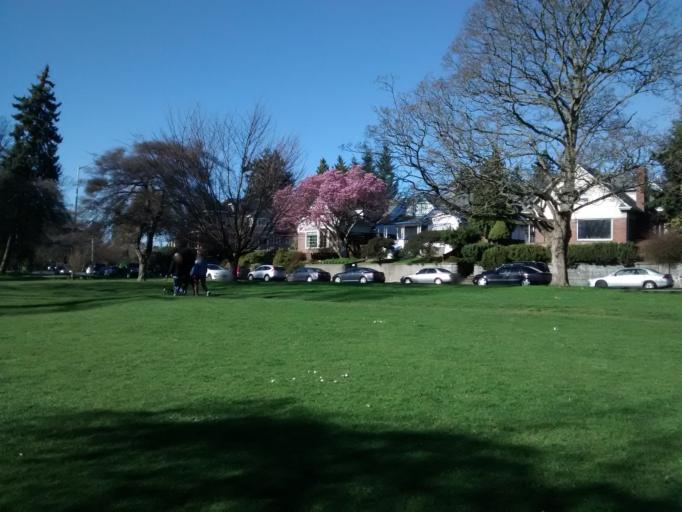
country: US
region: Washington
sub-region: King County
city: Shoreline
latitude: 47.6823
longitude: -122.3324
